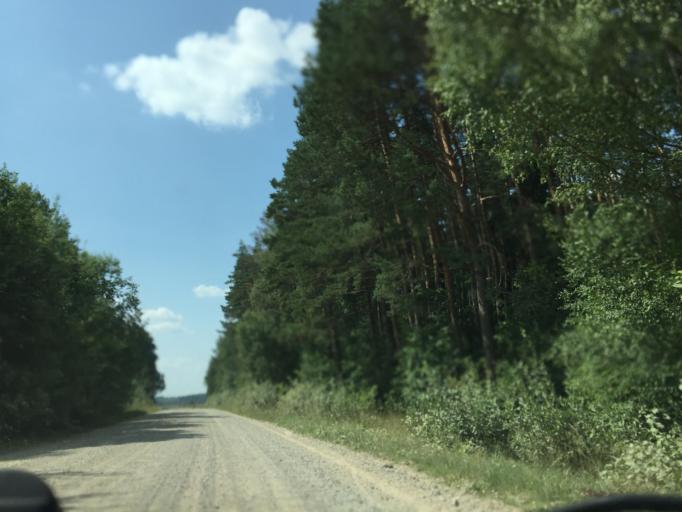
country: LT
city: Zagare
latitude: 56.3840
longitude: 23.2972
